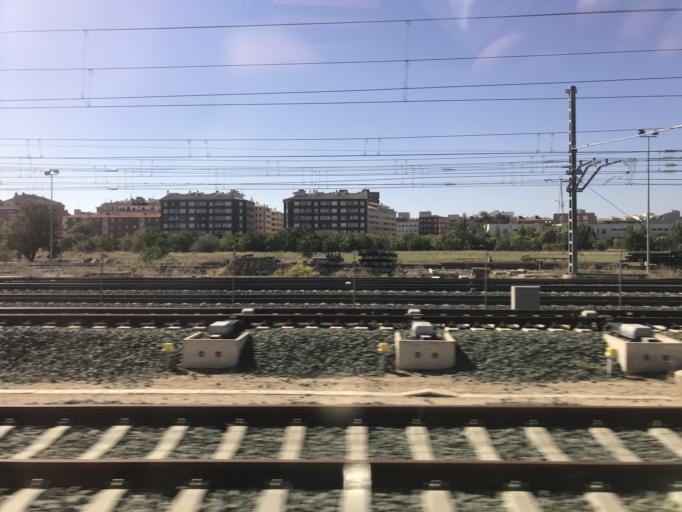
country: ES
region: Castille-La Mancha
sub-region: Provincia de Albacete
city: Albacete
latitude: 39.0032
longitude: -1.8503
